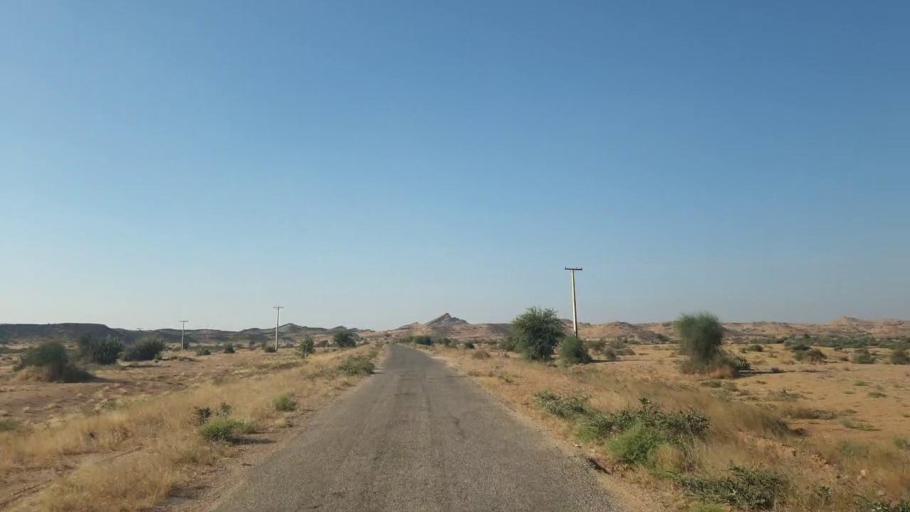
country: PK
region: Sindh
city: Malir Cantonment
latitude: 25.3972
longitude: 67.4941
